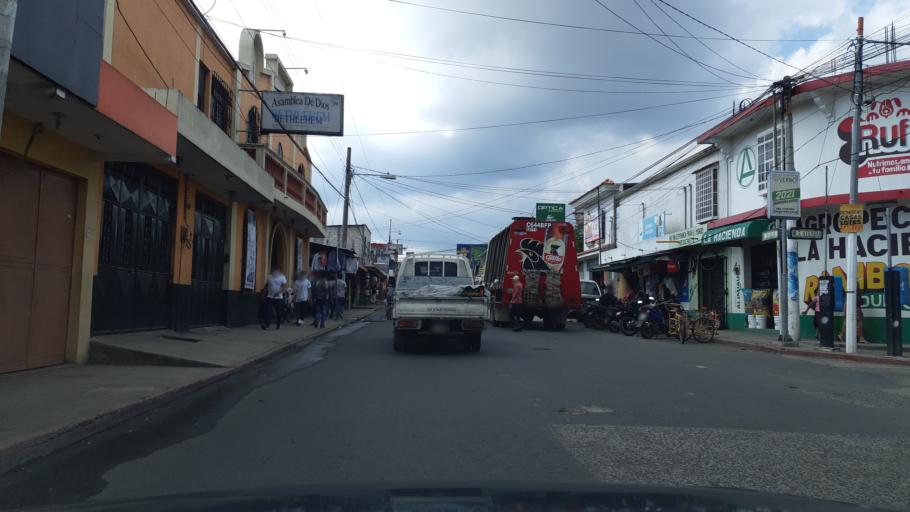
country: GT
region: Chimaltenango
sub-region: Municipio de Chimaltenango
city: Chimaltenango
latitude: 14.6614
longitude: -90.8129
